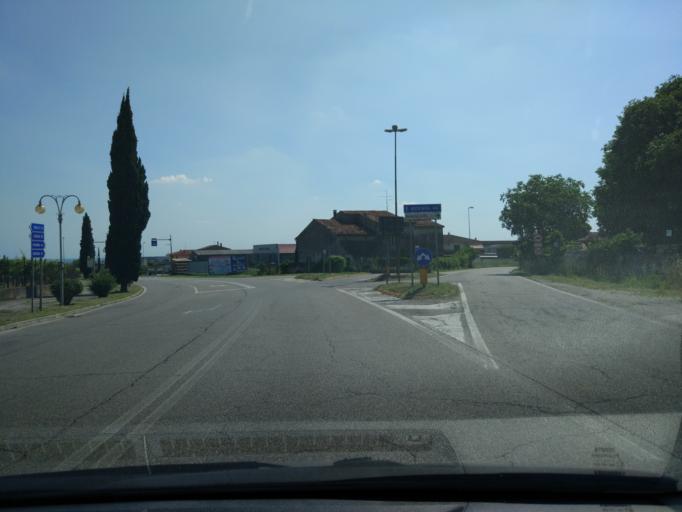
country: IT
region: Veneto
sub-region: Provincia di Verona
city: Illasi
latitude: 45.4620
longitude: 11.1773
